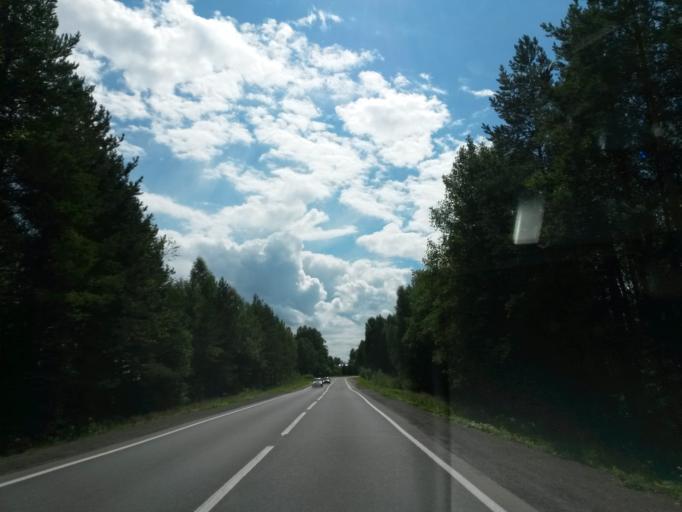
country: RU
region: Jaroslavl
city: Gavrilov-Yam
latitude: 57.2848
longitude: 39.9533
